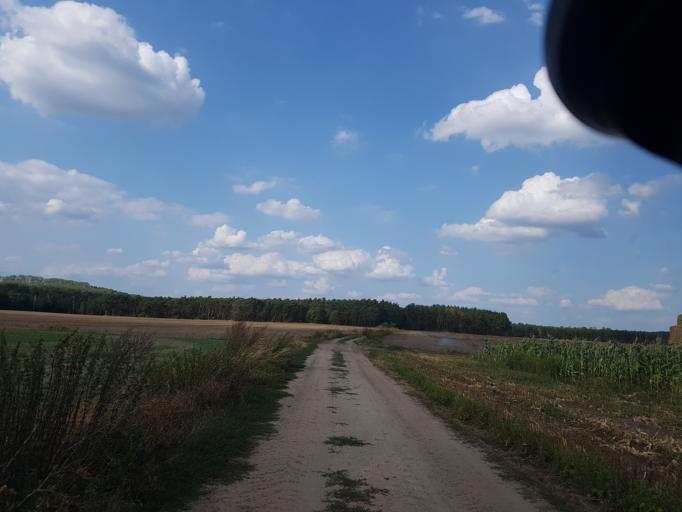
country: DE
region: Brandenburg
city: Calau
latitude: 51.7577
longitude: 13.9513
